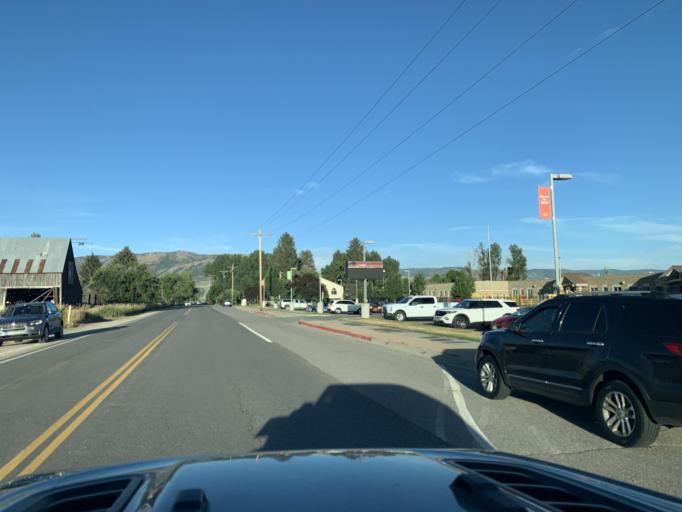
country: US
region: Utah
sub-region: Weber County
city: Wolf Creek
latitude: 41.2929
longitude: -111.8083
